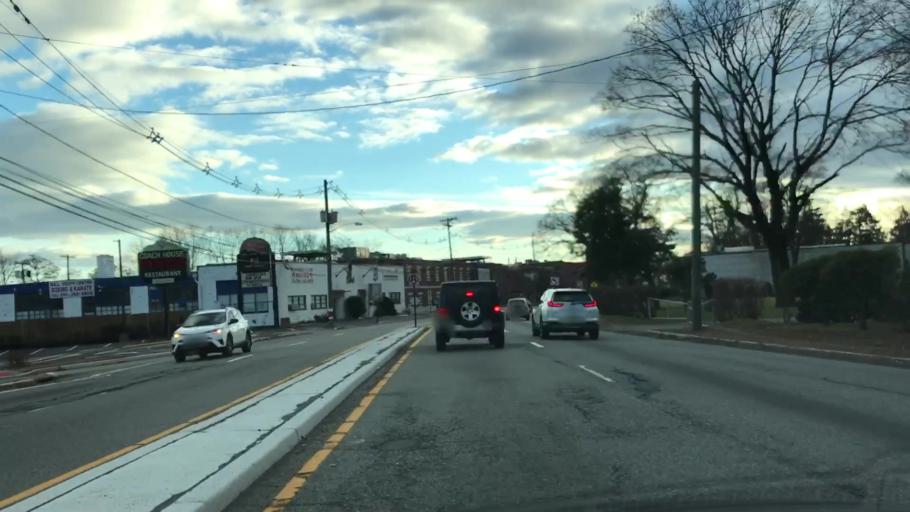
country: US
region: New Jersey
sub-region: Bergen County
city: Teaneck
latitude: 40.9050
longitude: -74.0334
